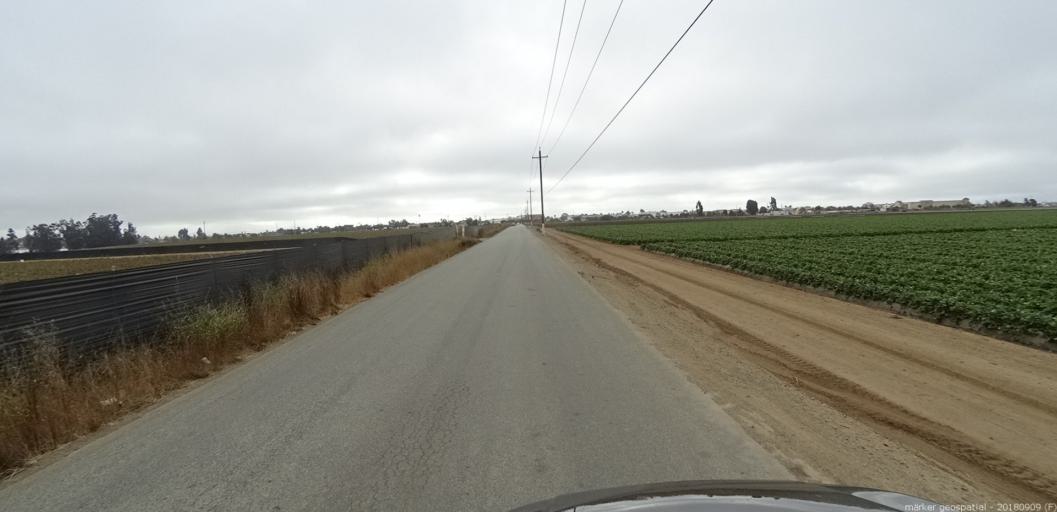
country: US
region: California
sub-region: Monterey County
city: Boronda
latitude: 36.7256
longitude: -121.6702
